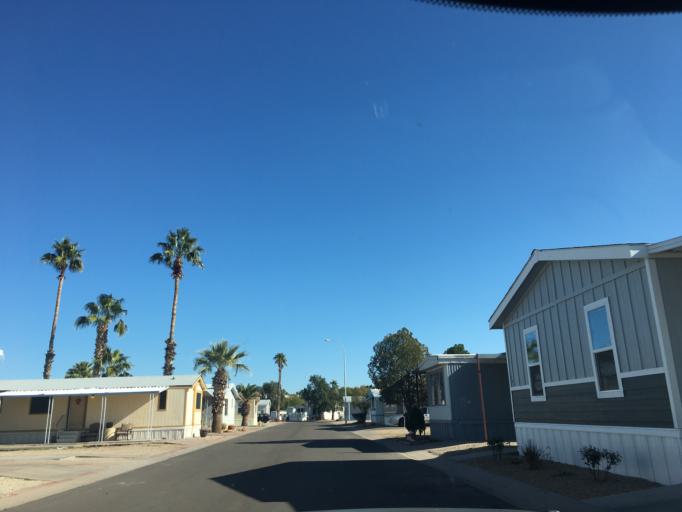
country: US
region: Arizona
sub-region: Maricopa County
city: Mesa
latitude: 33.4484
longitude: -111.8452
